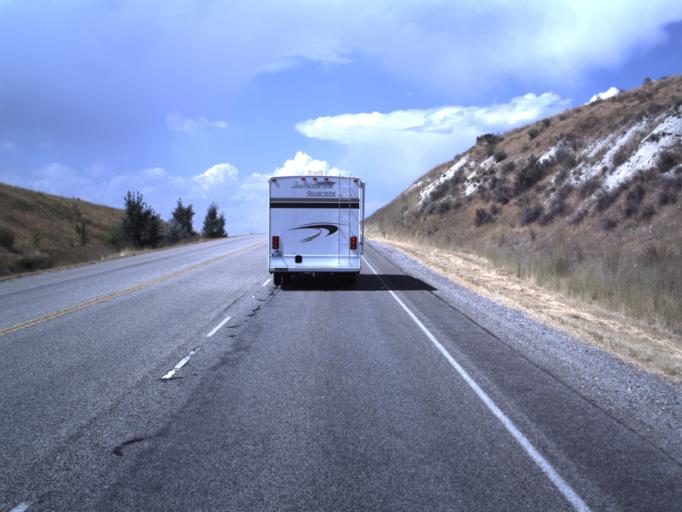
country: US
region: Utah
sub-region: Cache County
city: Mendon
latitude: 41.7675
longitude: -112.0128
